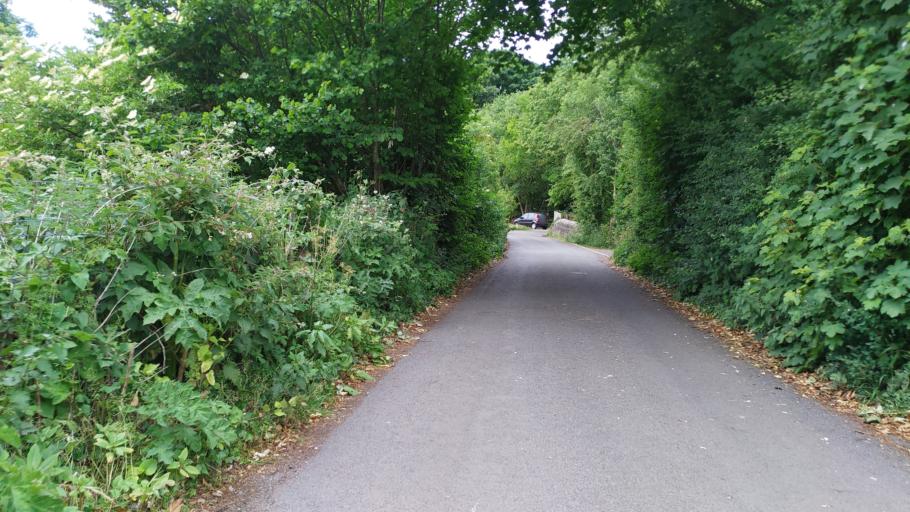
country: GB
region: England
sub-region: Lancashire
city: Clayton-le-Woods
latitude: 53.6880
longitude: -2.6423
